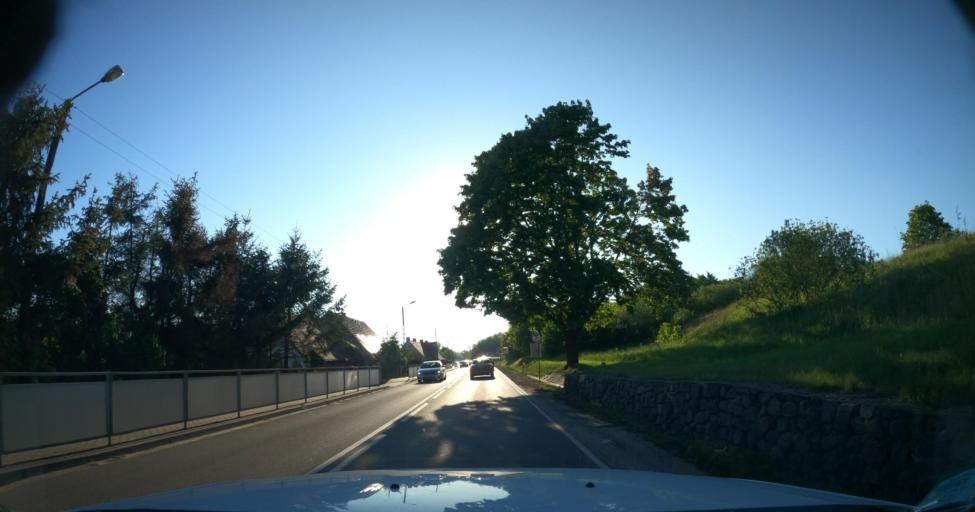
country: PL
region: Pomeranian Voivodeship
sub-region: Powiat kartuski
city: Zukowo
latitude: 54.3381
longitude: 18.4008
